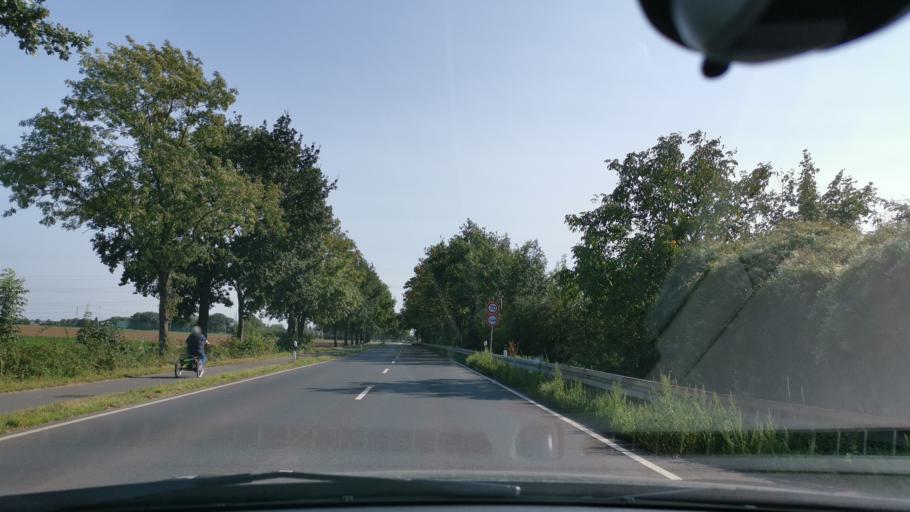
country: DE
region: North Rhine-Westphalia
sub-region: Regierungsbezirk Dusseldorf
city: Grevenbroich
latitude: 51.0835
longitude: 6.6276
